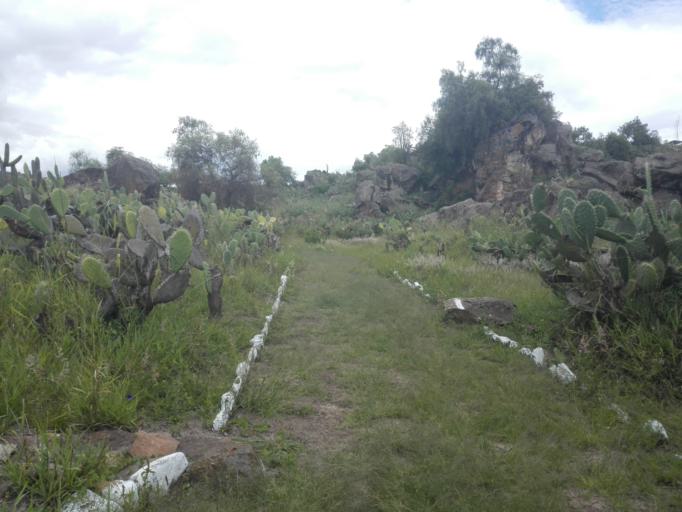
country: PE
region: Ayacucho
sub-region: Provincia de Huamanga
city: Pacaycasa
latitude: -13.0652
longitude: -74.1926
